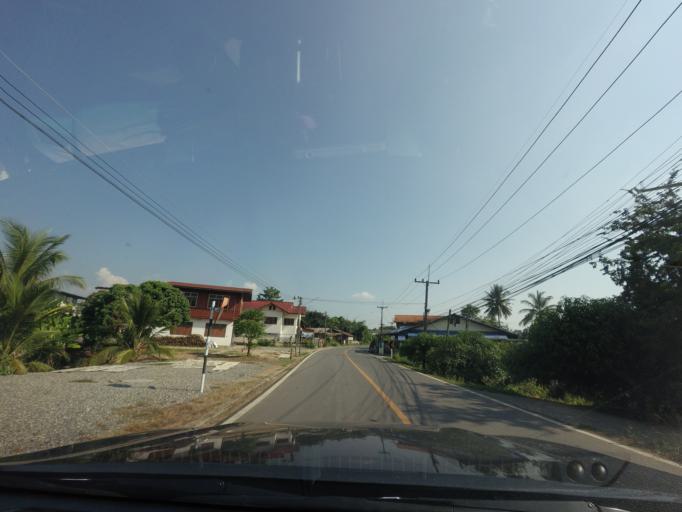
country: TH
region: Nan
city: Nan
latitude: 18.8544
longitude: 100.8111
